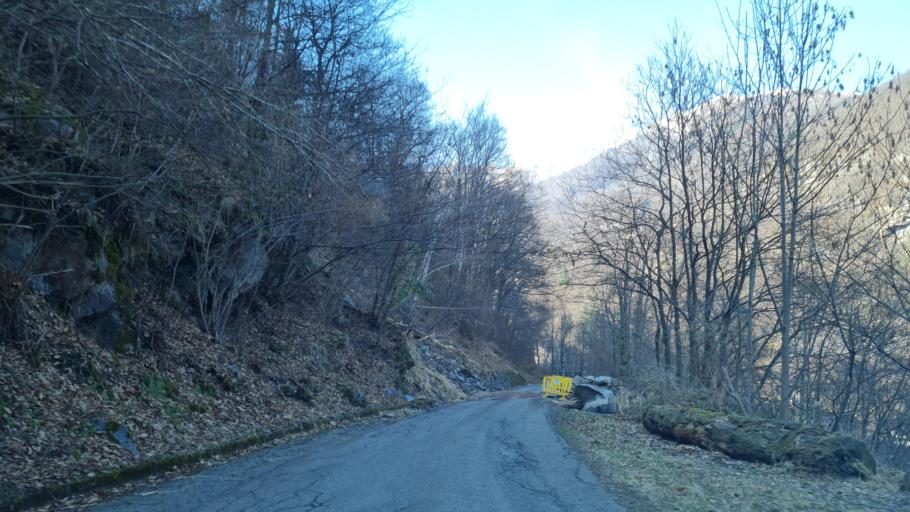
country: IT
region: Piedmont
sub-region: Provincia di Biella
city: San Paolo Cervo
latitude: 45.6450
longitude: 8.0172
